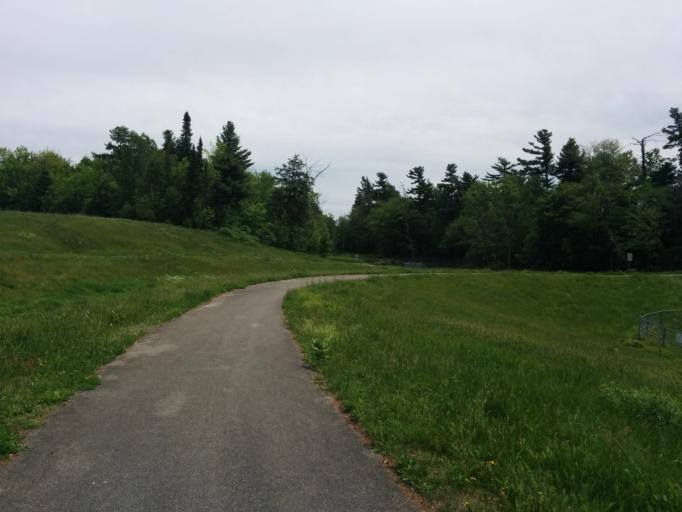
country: CA
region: Ontario
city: Clarence-Rockland
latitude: 45.4853
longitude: -75.4676
